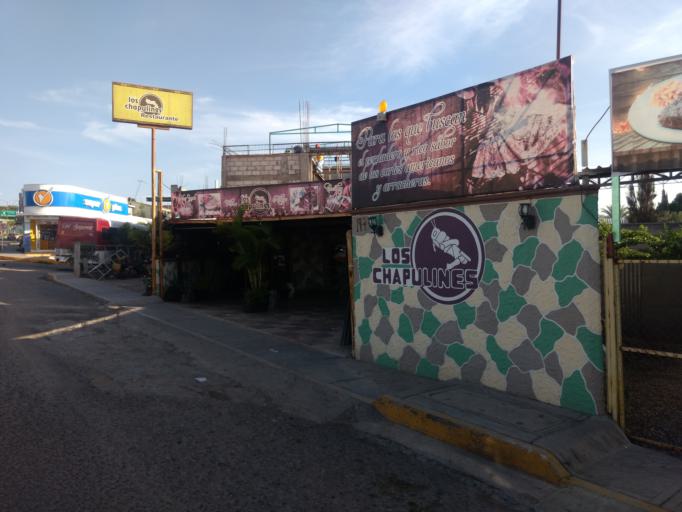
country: MX
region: Oaxaca
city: Ciudad de Huajuapam de Leon
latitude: 17.8143
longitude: -97.7882
